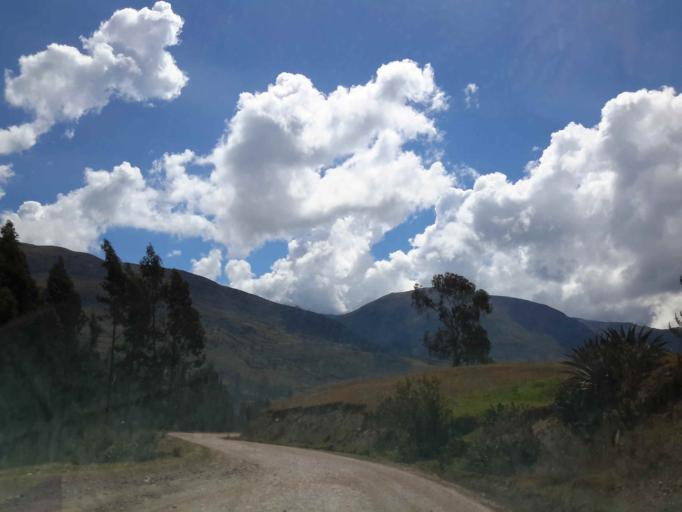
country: PE
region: Apurimac
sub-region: Provincia de Andahuaylas
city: Pacucha
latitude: -13.6204
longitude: -73.3339
